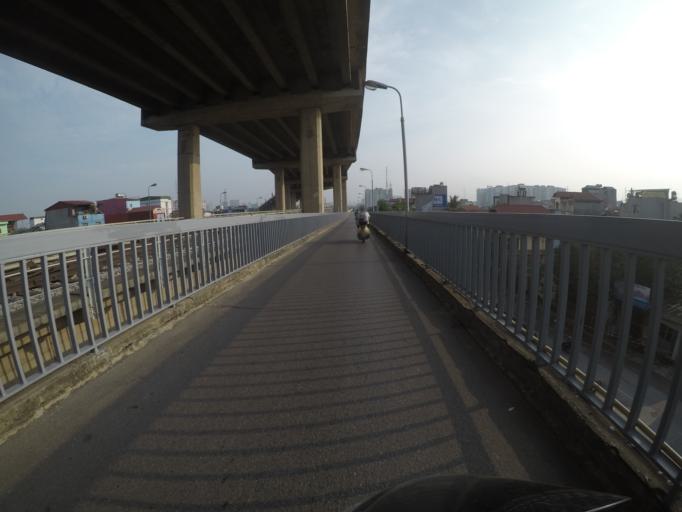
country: VN
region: Ha Noi
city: Tay Ho
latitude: 21.0907
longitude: 105.7858
